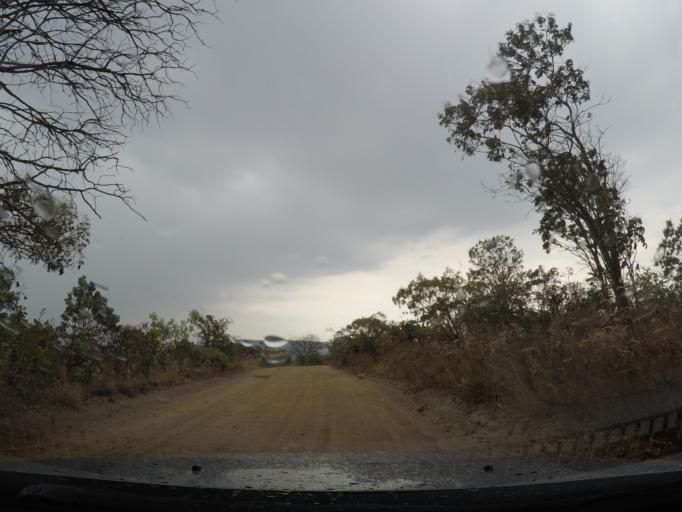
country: BR
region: Goias
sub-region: Pirenopolis
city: Pirenopolis
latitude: -15.8228
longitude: -48.9068
